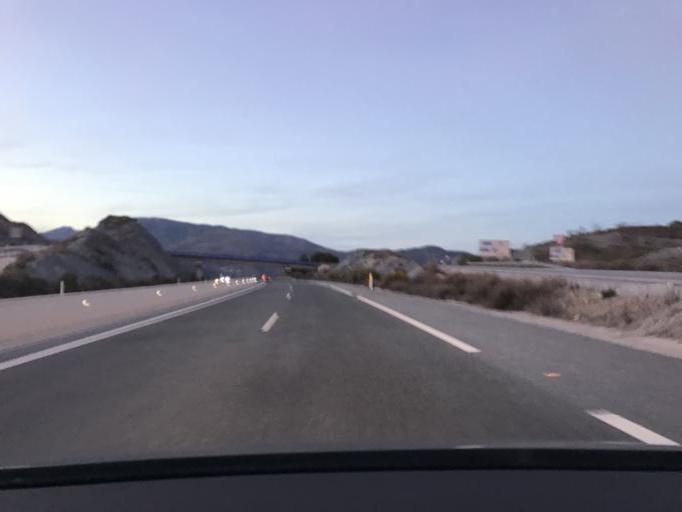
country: ES
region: Andalusia
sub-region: Provincia de Granada
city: Velez de Benaudalla
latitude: 36.8036
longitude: -3.5091
